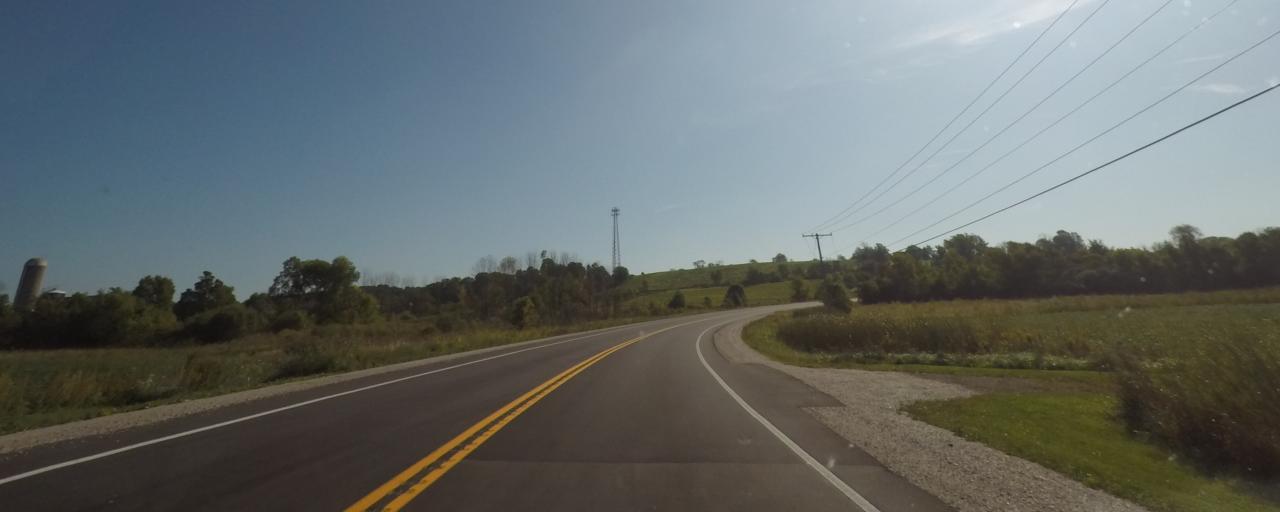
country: US
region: Wisconsin
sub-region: Jefferson County
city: Johnson Creek
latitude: 43.0196
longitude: -88.7154
